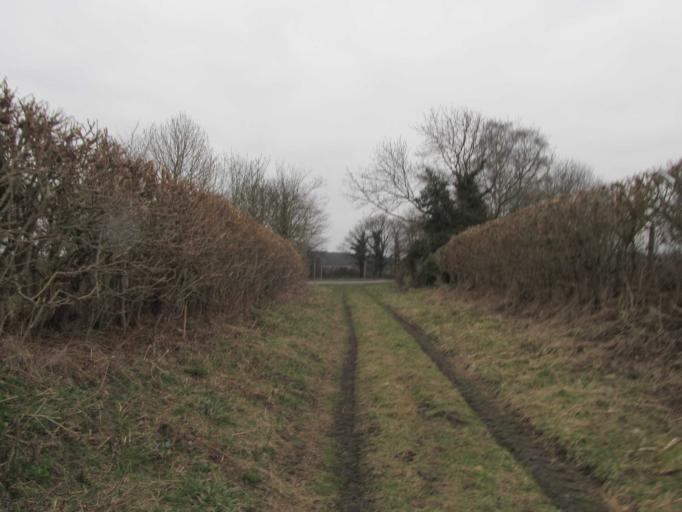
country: GB
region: England
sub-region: Doncaster
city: Bawtry
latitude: 53.4192
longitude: -1.0000
